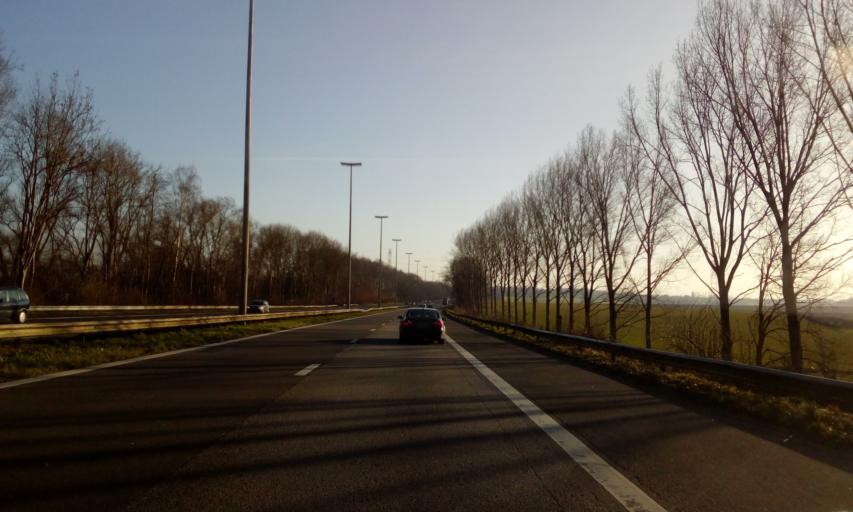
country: BE
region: Wallonia
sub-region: Province du Hainaut
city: Pont-a-Celles
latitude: 50.5561
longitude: 4.3611
